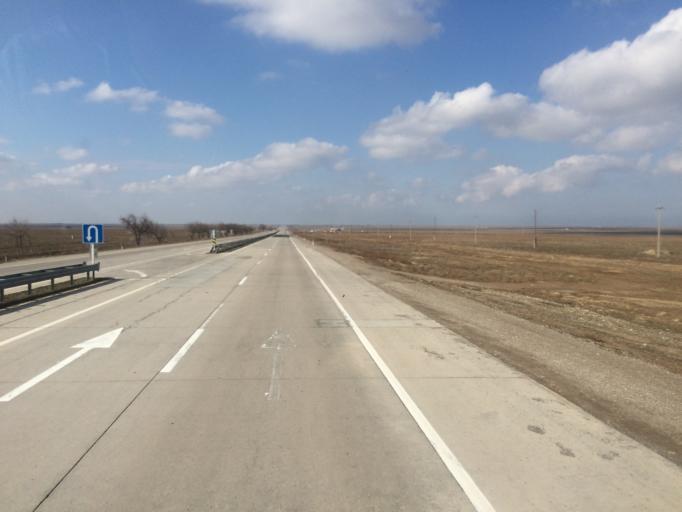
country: KZ
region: Ongtustik Qazaqstan
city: Temirlanovka
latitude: 42.8333
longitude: 69.1221
